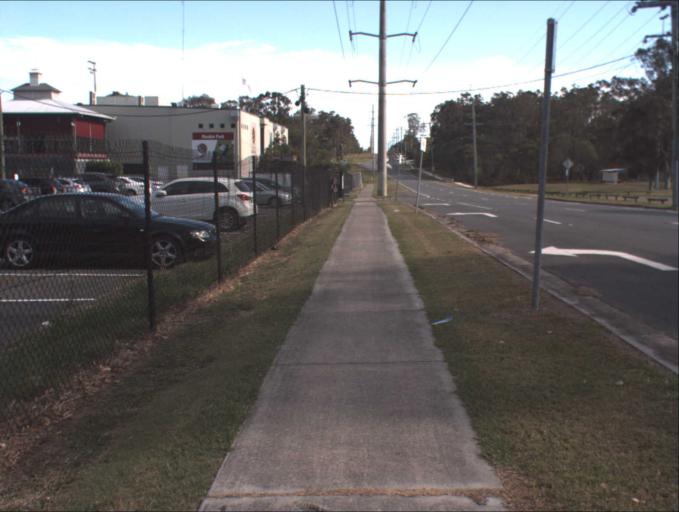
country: AU
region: Queensland
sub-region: Logan
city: Slacks Creek
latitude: -27.6456
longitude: 153.1364
